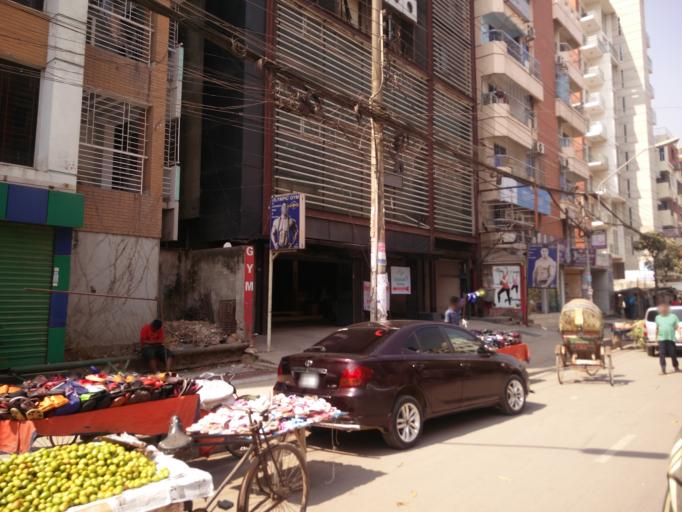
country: BD
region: Dhaka
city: Tungi
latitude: 23.8764
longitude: 90.3908
